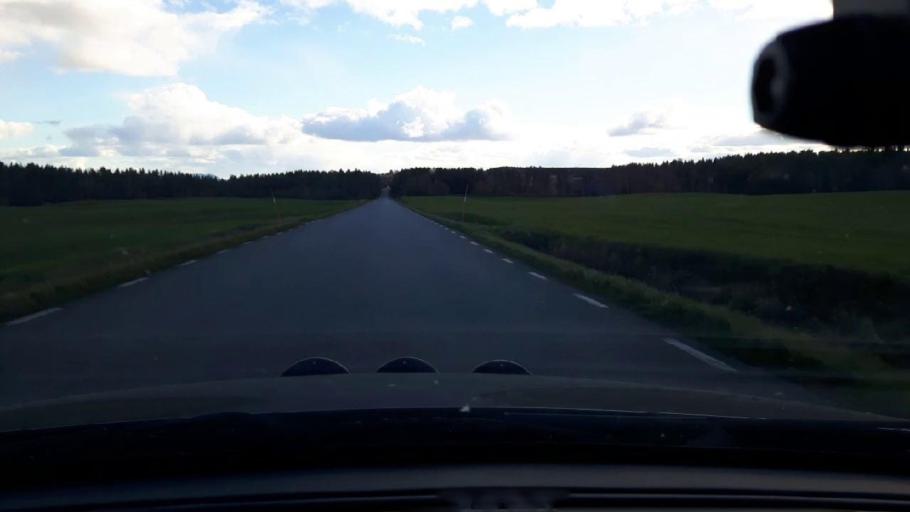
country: SE
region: Jaemtland
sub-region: Bergs Kommun
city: Hoverberg
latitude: 63.0332
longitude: 14.3452
